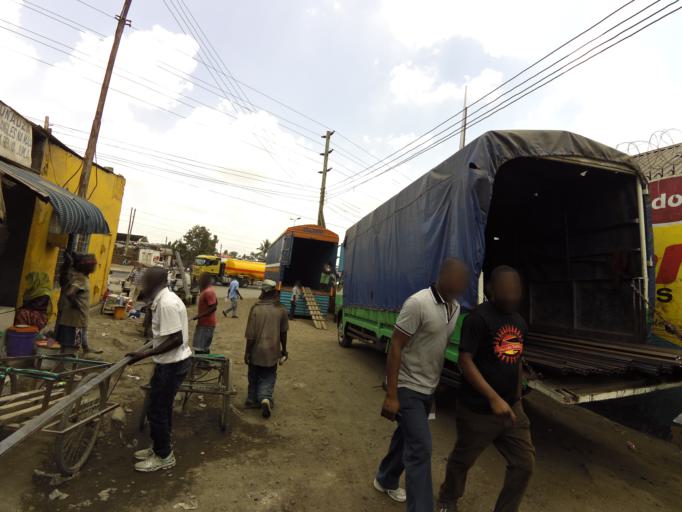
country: TZ
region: Dar es Salaam
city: Dar es Salaam
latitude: -6.8358
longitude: 39.2421
